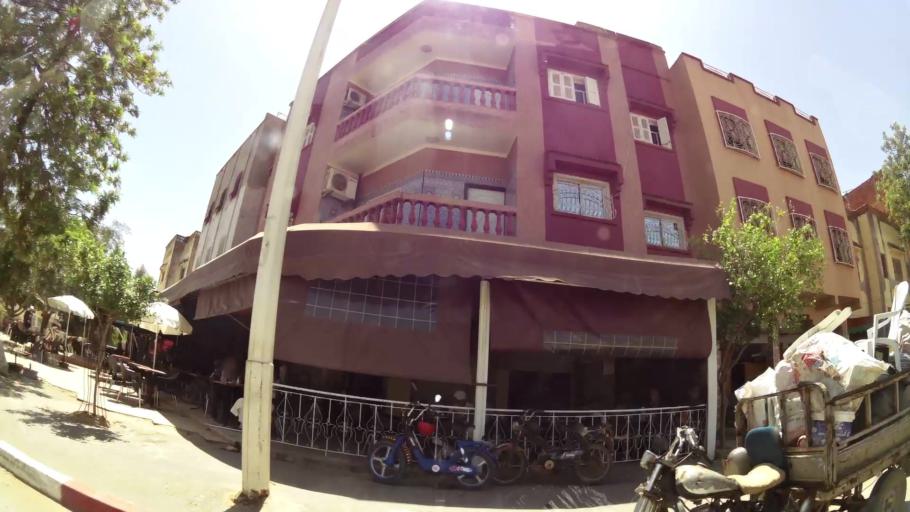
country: MA
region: Rabat-Sale-Zemmour-Zaer
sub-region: Khemisset
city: Khemisset
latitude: 33.8361
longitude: -6.0679
